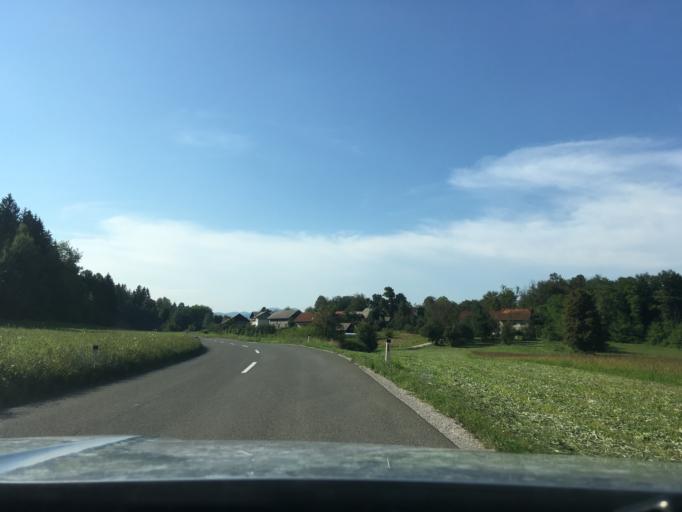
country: SI
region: Crnomelj
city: Crnomelj
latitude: 45.5054
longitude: 15.1897
